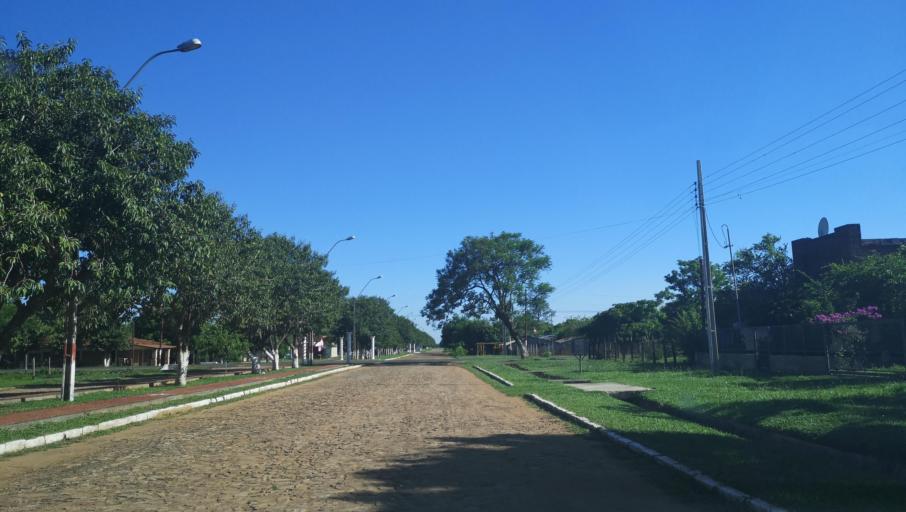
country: PY
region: Caaguazu
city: Carayao
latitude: -25.1956
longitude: -56.3997
